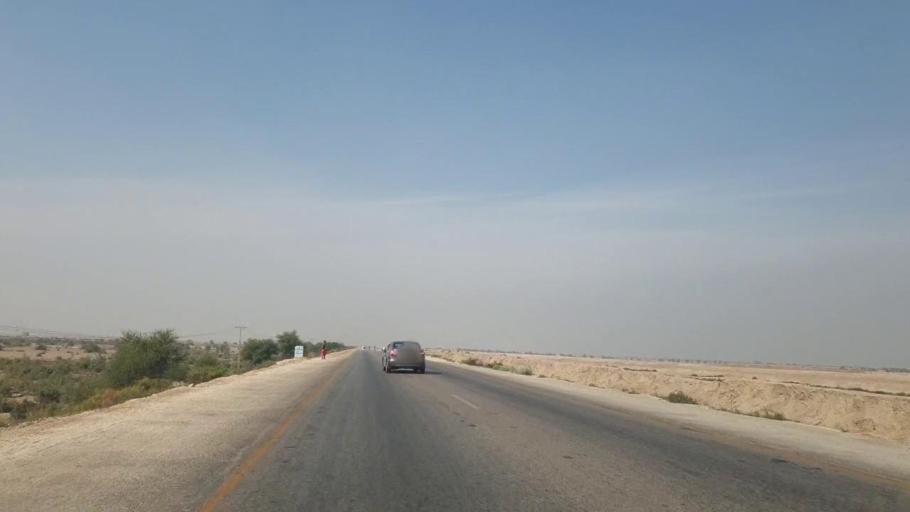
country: PK
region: Sindh
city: Sann
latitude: 25.9055
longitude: 68.2290
